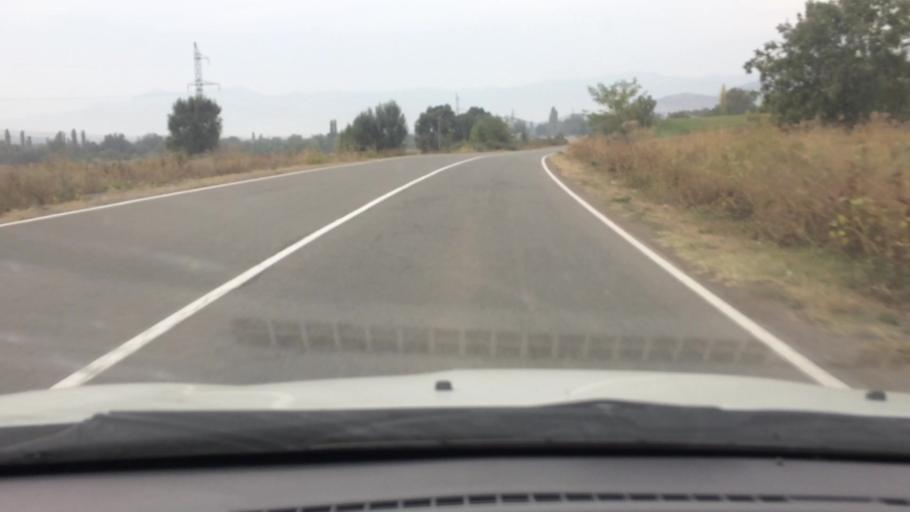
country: GE
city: Naghvarevi
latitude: 41.3144
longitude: 44.7933
